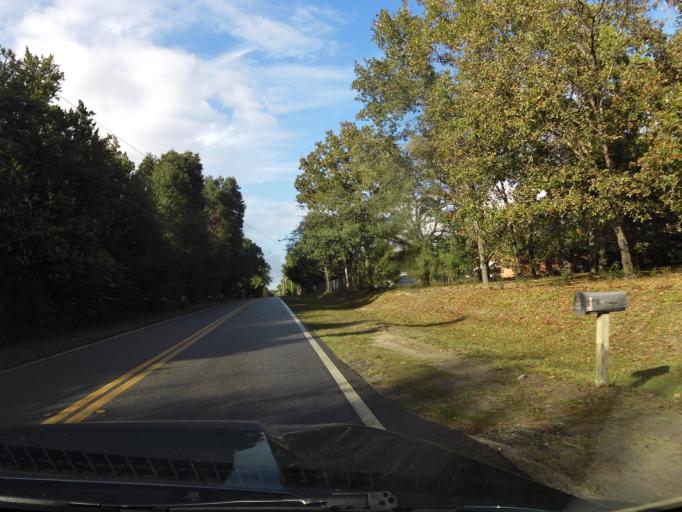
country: US
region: Florida
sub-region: Clay County
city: Asbury Lake
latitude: 30.0363
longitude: -81.8467
